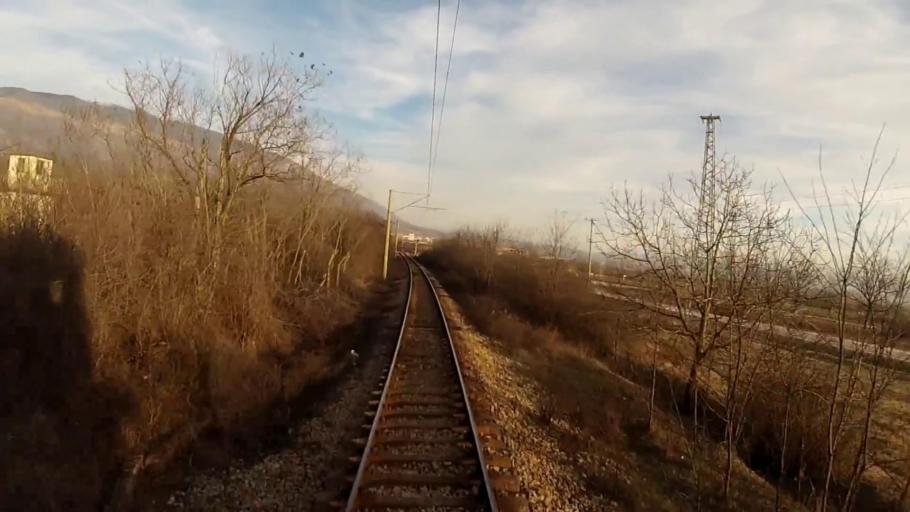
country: BG
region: Plovdiv
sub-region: Obshtina Karlovo
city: Karlovo
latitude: 42.6313
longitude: 24.7804
